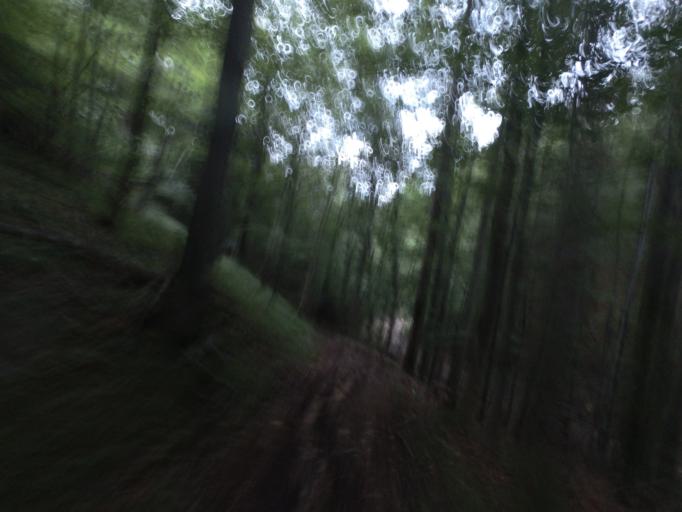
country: AT
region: Salzburg
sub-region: Politischer Bezirk Salzburg-Umgebung
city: Grodig
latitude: 47.7396
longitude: 13.0298
